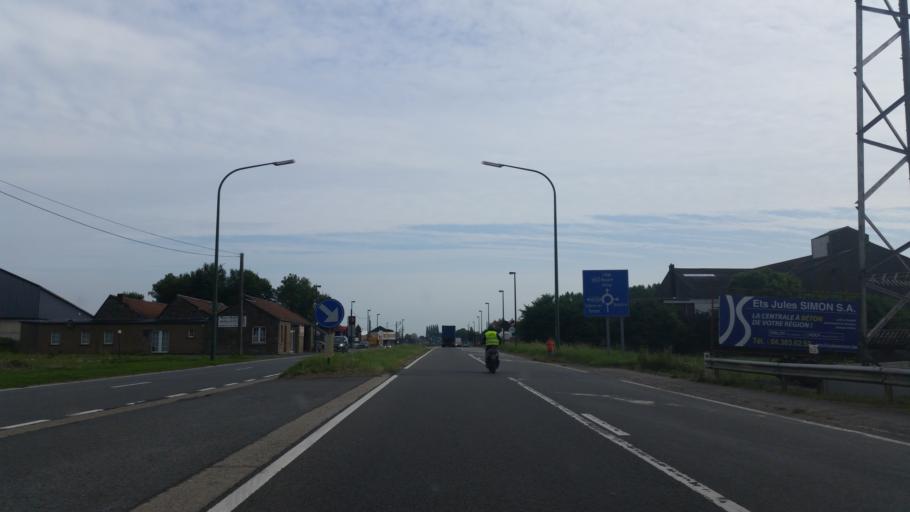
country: BE
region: Wallonia
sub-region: Province de Liege
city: Nandrin
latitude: 50.5041
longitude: 5.3954
